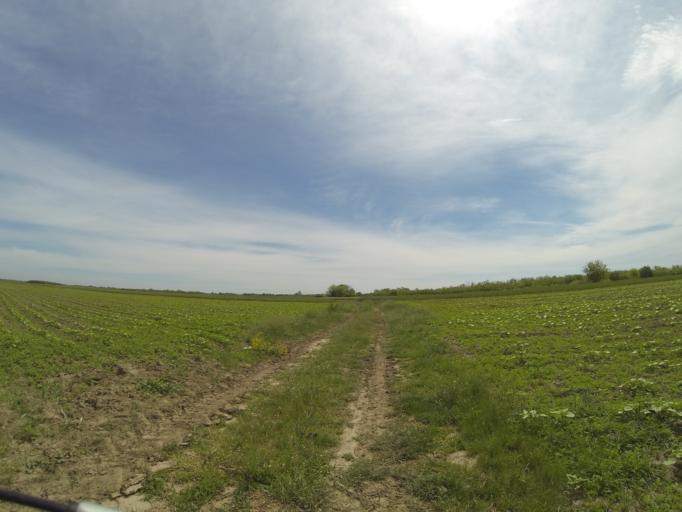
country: RO
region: Dolj
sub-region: Comuna Leu
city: Leu
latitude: 44.1985
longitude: 23.9858
